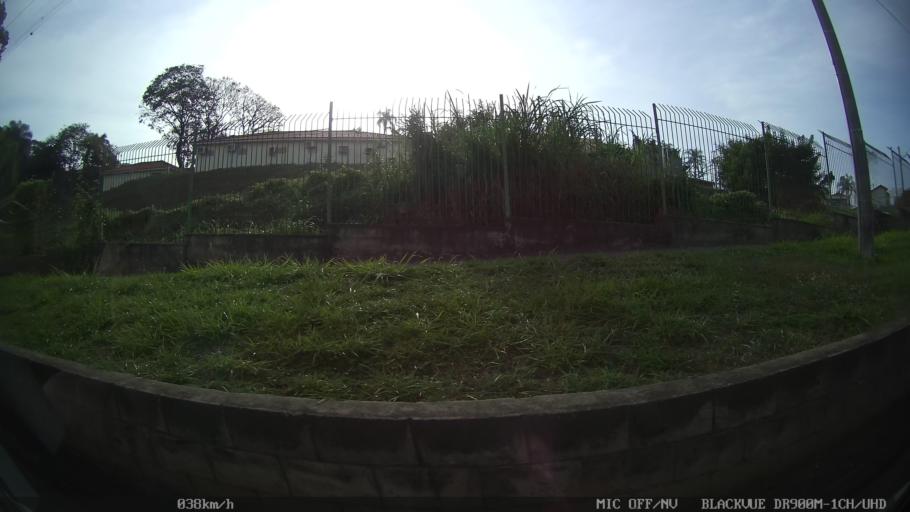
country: BR
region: Sao Paulo
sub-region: Piracicaba
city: Piracicaba
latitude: -22.7086
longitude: -47.6452
